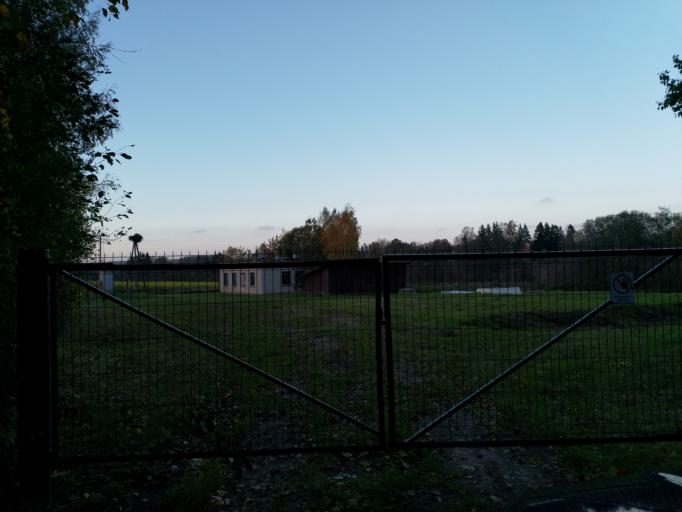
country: LV
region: Aizpute
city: Aizpute
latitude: 56.8388
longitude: 21.7745
